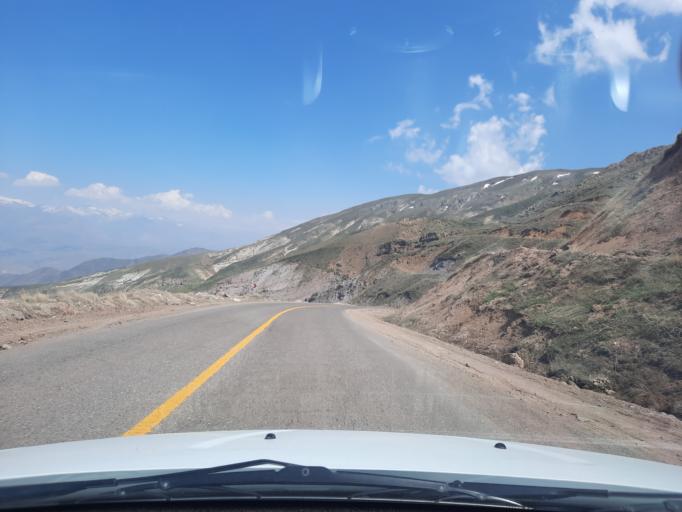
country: IR
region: Qazvin
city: Qazvin
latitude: 36.3960
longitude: 50.2129
